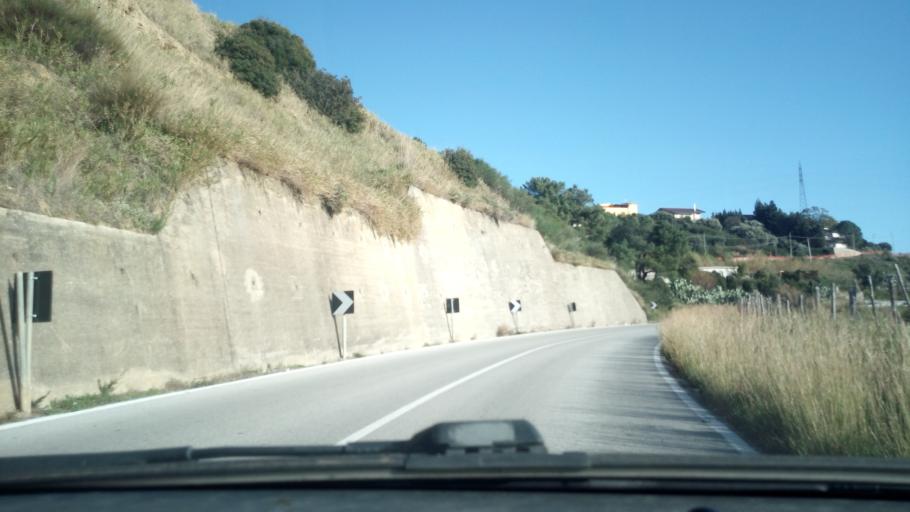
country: IT
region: Calabria
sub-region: Provincia di Catanzaro
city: Roccelletta
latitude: 38.8309
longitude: 16.5964
